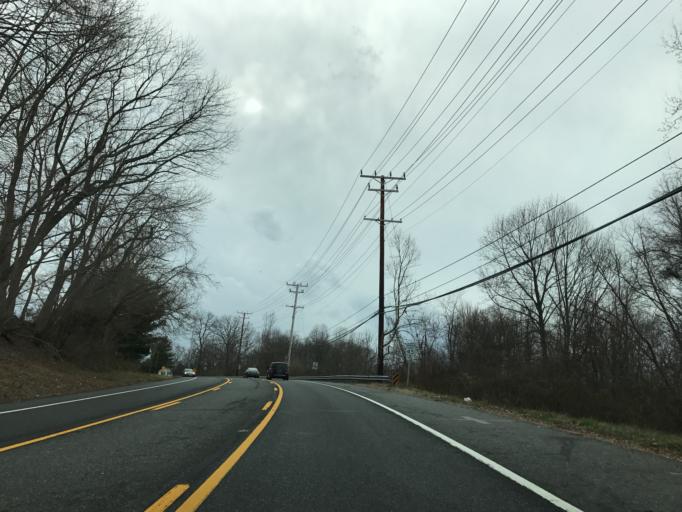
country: US
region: Maryland
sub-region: Harford County
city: North Bel Air
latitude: 39.5152
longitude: -76.3699
